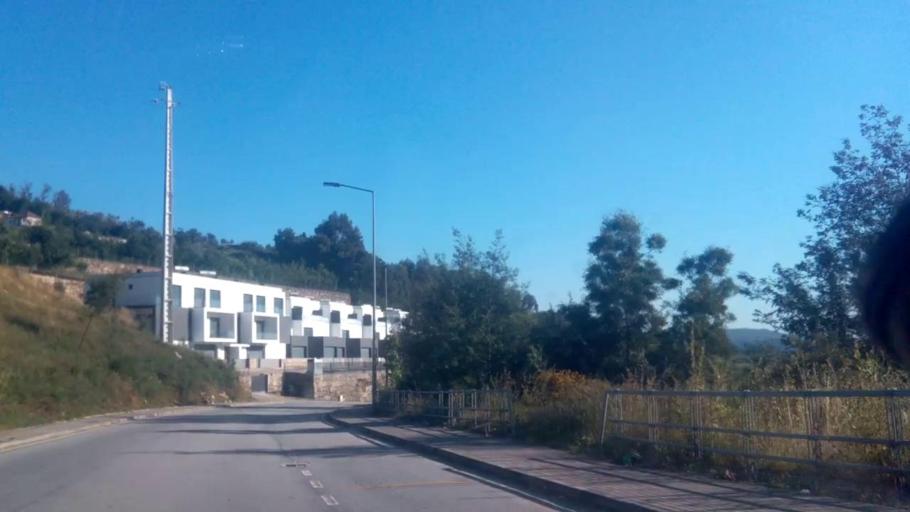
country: PT
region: Porto
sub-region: Penafiel
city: Penafiel
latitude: 41.1981
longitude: -8.2848
